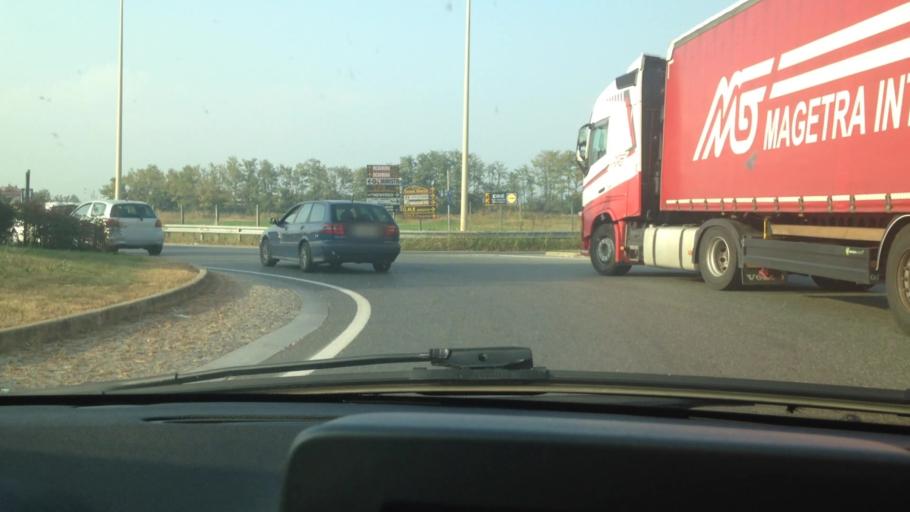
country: IT
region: Piedmont
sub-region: Provincia di Torino
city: Cirie
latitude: 45.2154
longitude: 7.6127
